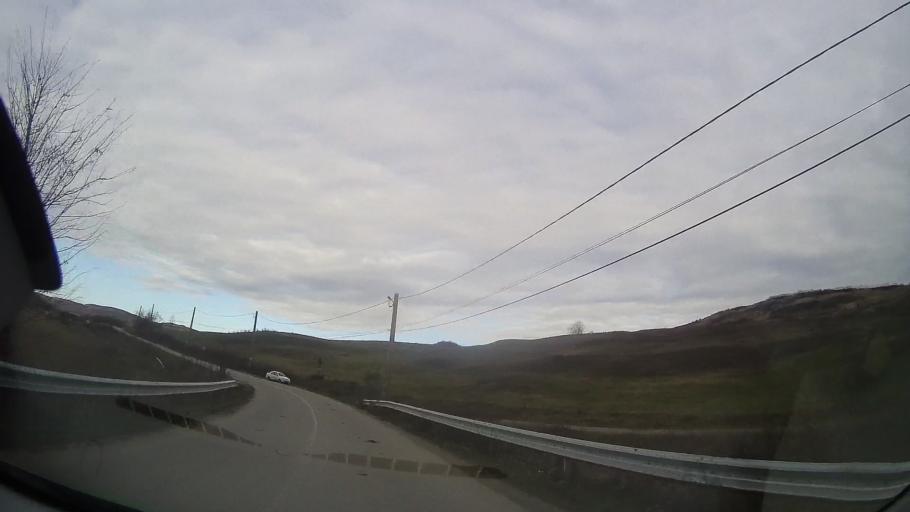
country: RO
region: Cluj
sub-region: Comuna Geaca
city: Geaca
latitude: 46.8326
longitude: 24.1351
